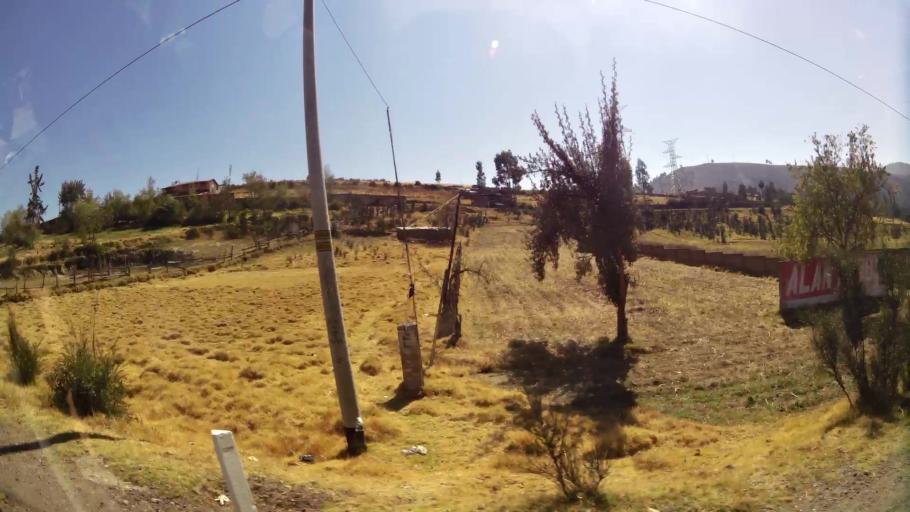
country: PE
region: Junin
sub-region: Provincia de Concepcion
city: Concepcion
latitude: -11.9372
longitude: -75.3127
